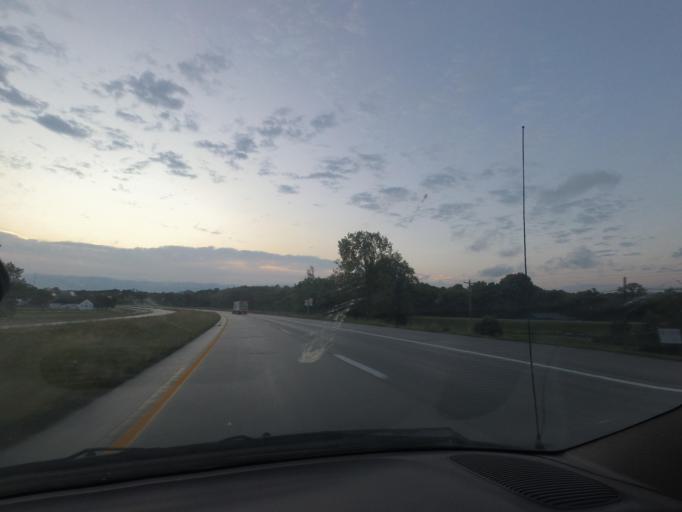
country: US
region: Missouri
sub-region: Macon County
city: Macon
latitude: 39.7467
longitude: -92.4972
